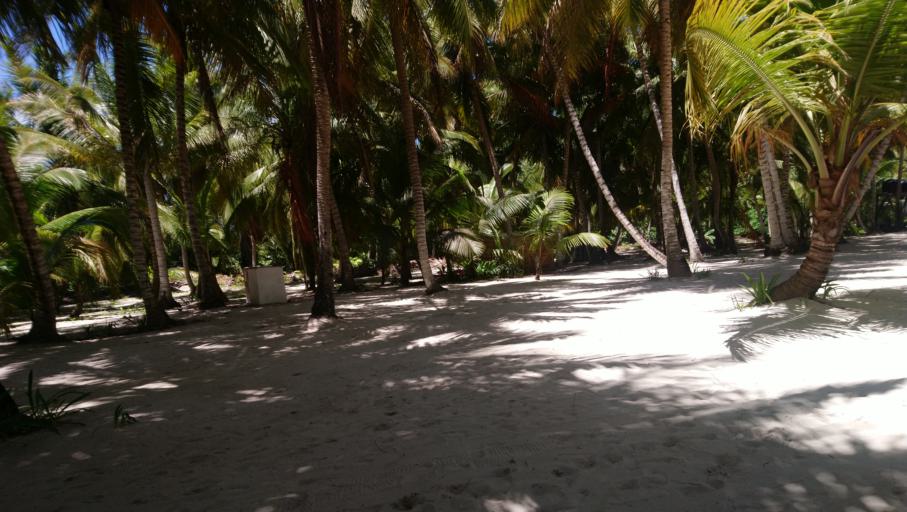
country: DO
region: La Altagracia
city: Boca de Yuma
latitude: 18.1723
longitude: -68.7817
